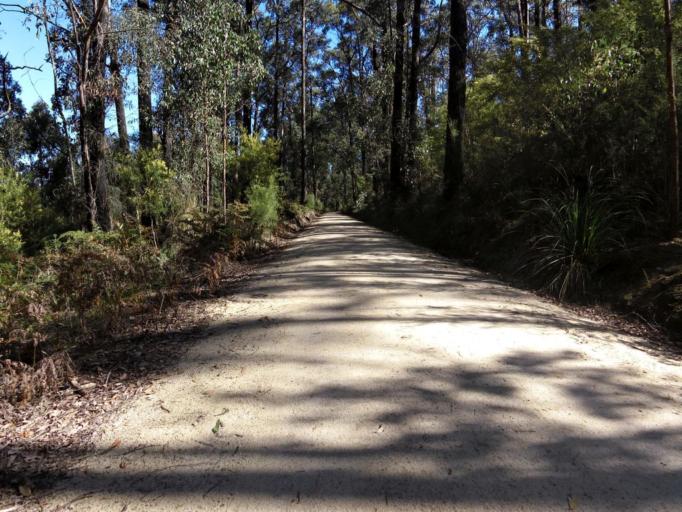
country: AU
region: Victoria
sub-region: Latrobe
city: Moe
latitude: -38.3860
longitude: 146.1896
